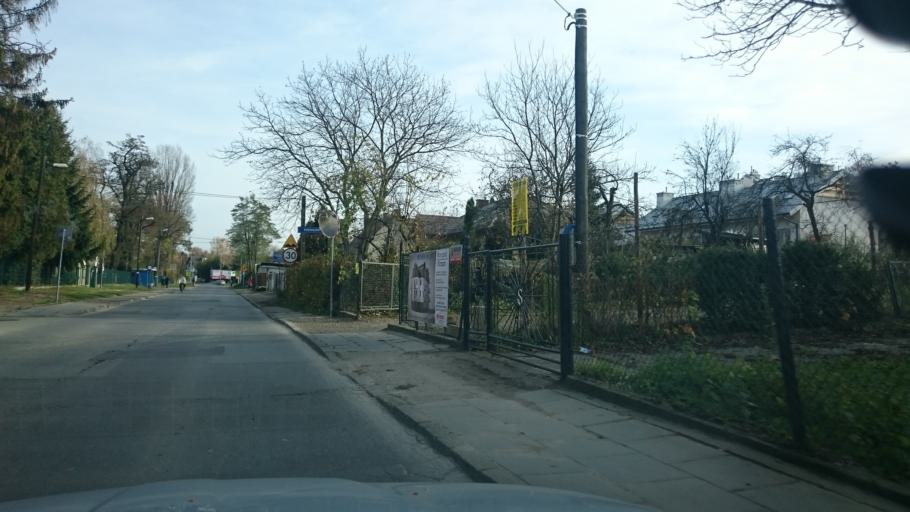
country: PL
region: Lesser Poland Voivodeship
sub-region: Powiat wielicki
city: Czarnochowice
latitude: 50.0221
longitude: 20.0060
